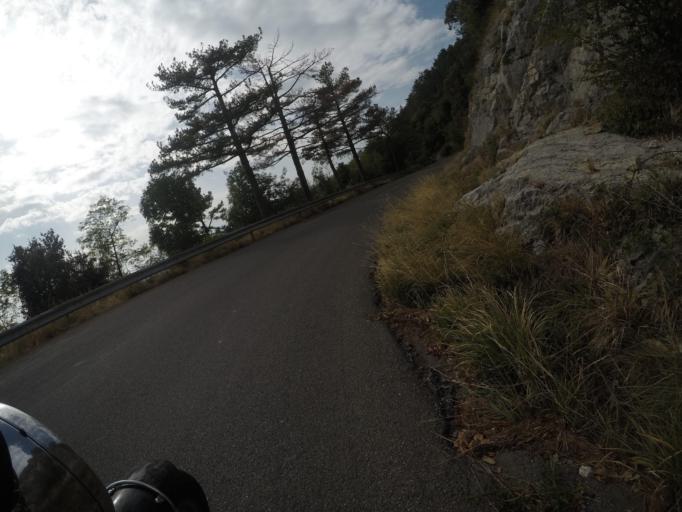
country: IT
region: Liguria
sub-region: Provincia di La Spezia
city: Casano-Dogana-Isola
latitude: 44.1202
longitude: 10.0835
